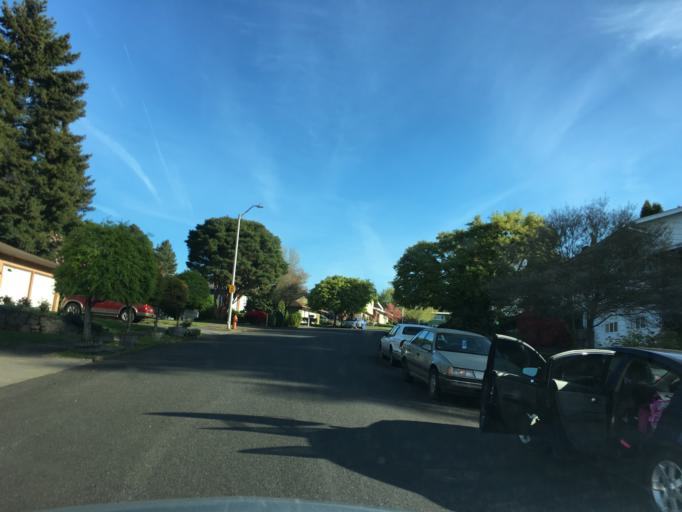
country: US
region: Oregon
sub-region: Multnomah County
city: Lents
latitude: 45.5509
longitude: -122.5227
